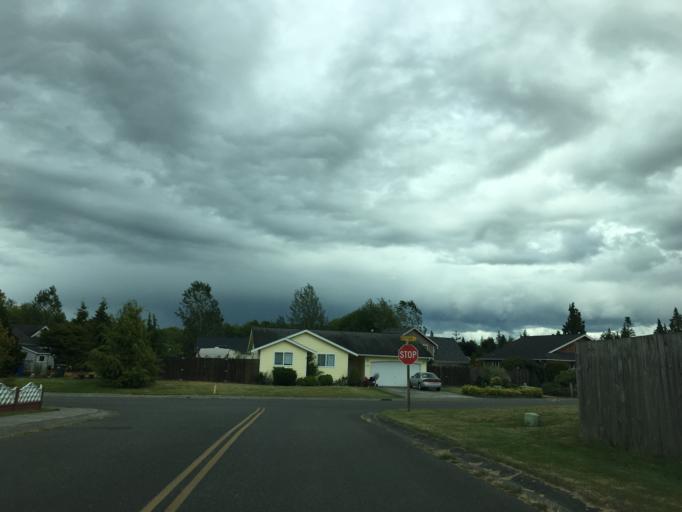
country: US
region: Washington
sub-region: Whatcom County
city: Birch Bay
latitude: 48.9491
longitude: -122.7418
